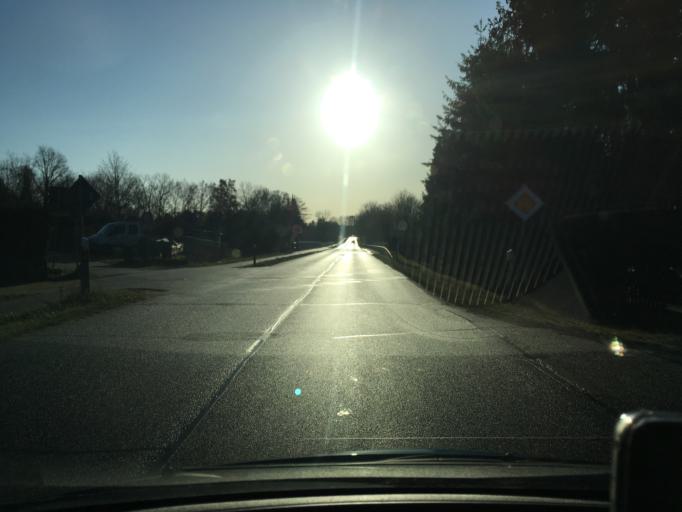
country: DE
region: Lower Saxony
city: Wendisch Evern
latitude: 53.2187
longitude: 10.4639
